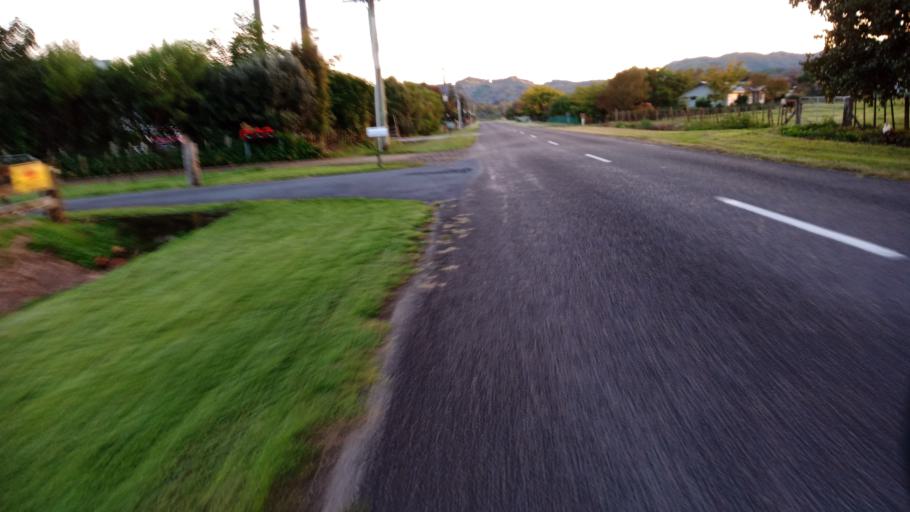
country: NZ
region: Gisborne
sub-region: Gisborne District
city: Gisborne
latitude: -38.6372
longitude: 177.9851
